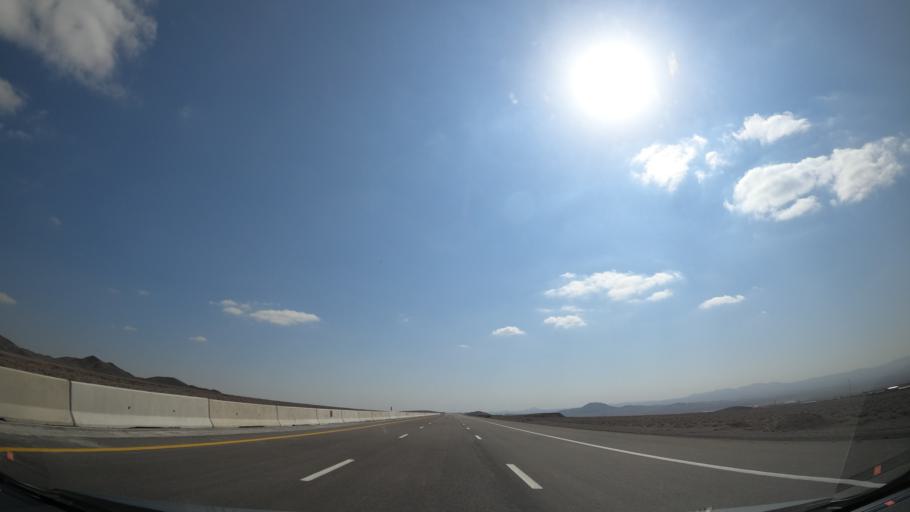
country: IR
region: Alborz
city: Eshtehard
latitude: 35.6719
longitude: 50.6453
